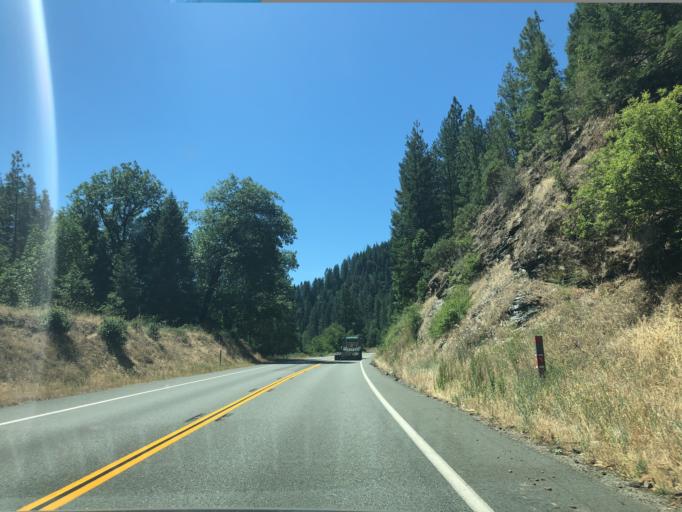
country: US
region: California
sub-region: Trinity County
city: Weaverville
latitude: 40.6723
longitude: -122.9437
